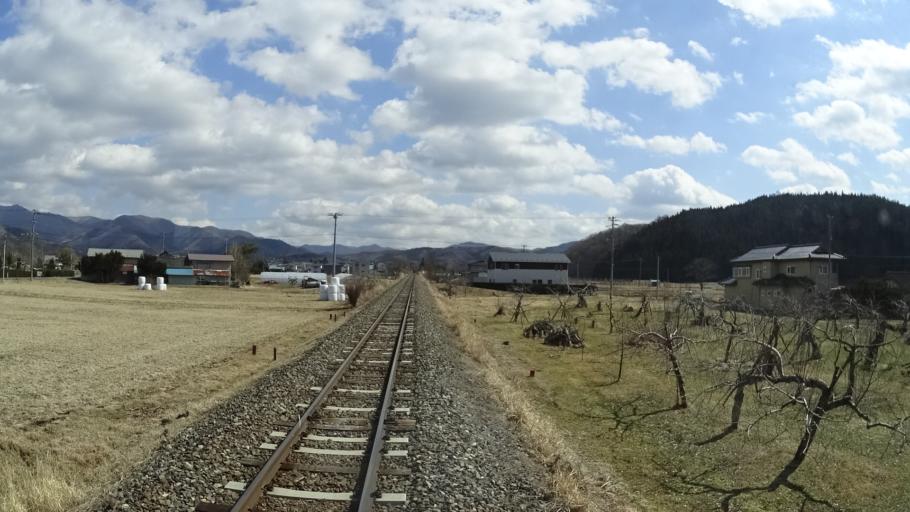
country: JP
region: Iwate
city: Tono
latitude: 39.2885
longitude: 141.5813
